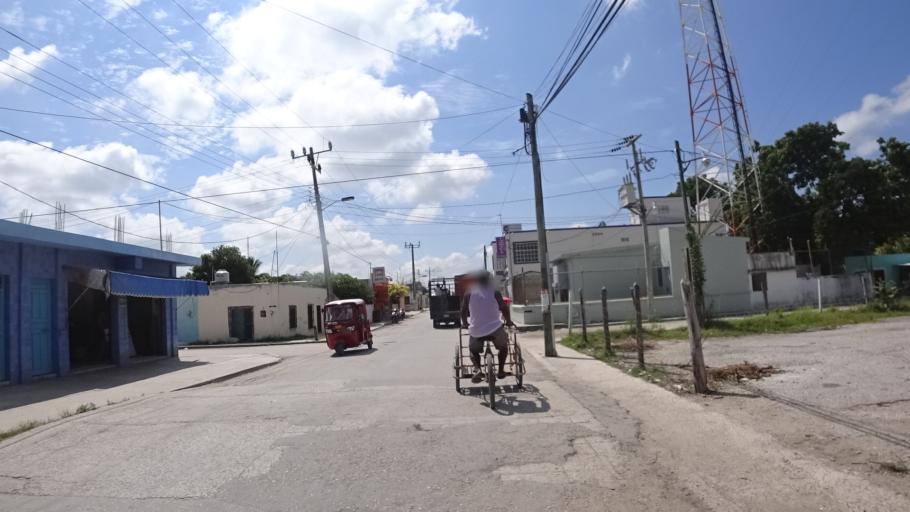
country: MX
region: Campeche
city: Sabancuy
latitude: 18.9722
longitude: -91.1793
